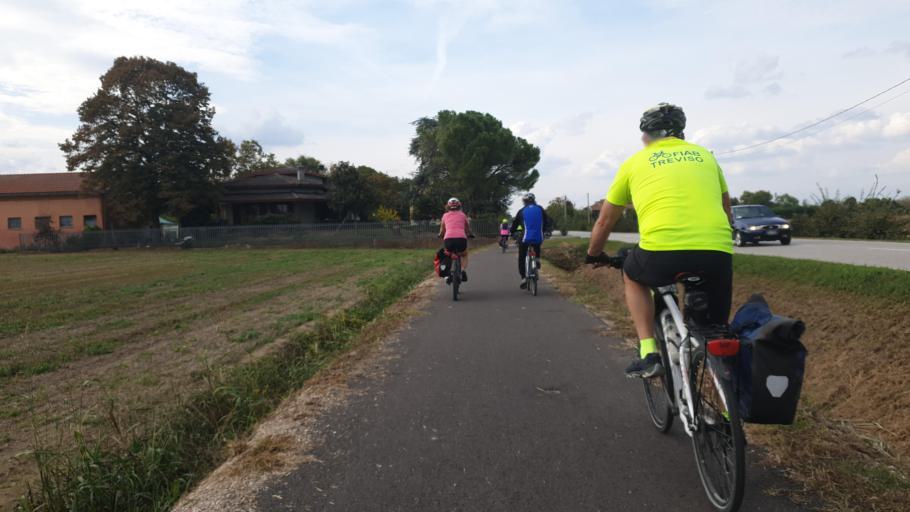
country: IT
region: Veneto
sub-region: Provincia di Vicenza
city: Poiana Maggiore
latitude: 45.2866
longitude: 11.5183
